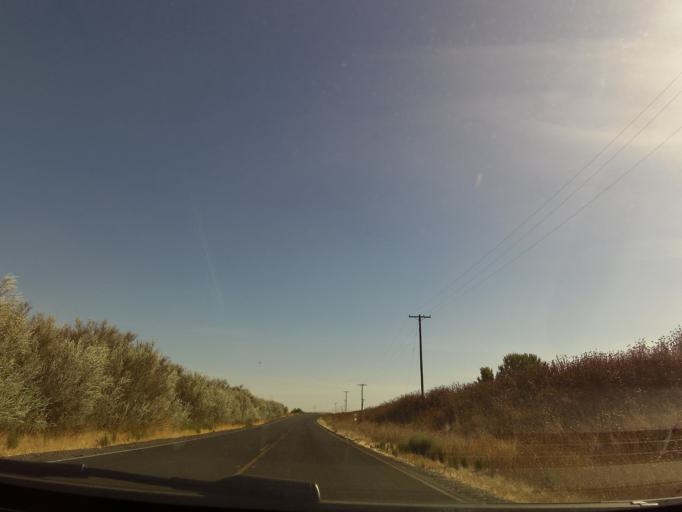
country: US
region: California
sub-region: San Joaquin County
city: Mountain House
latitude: 37.8573
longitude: -121.4489
